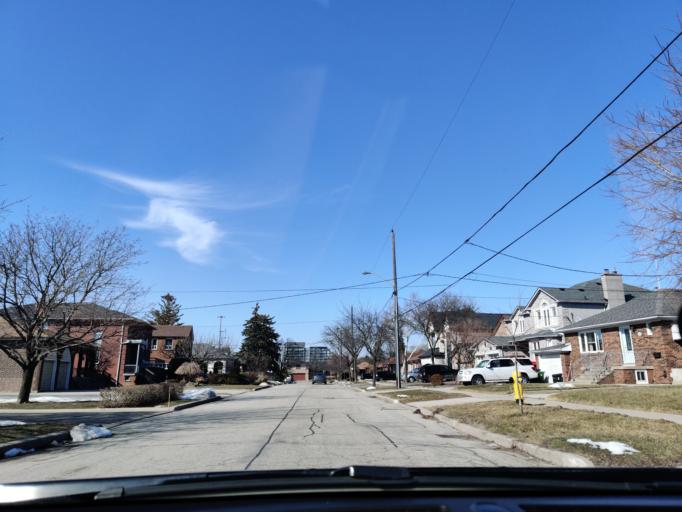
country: CA
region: Ontario
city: Toronto
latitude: 43.7208
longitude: -79.4781
